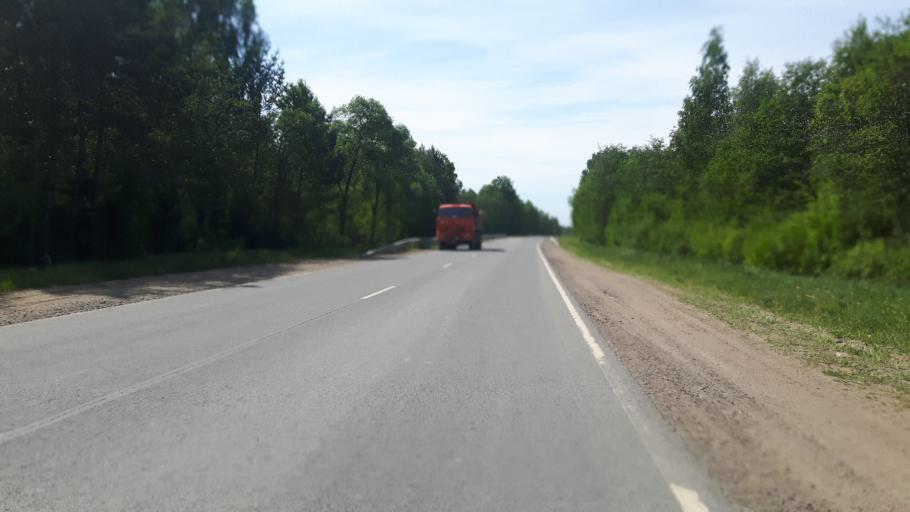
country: RU
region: Leningrad
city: Vistino
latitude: 59.6814
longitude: 28.4568
